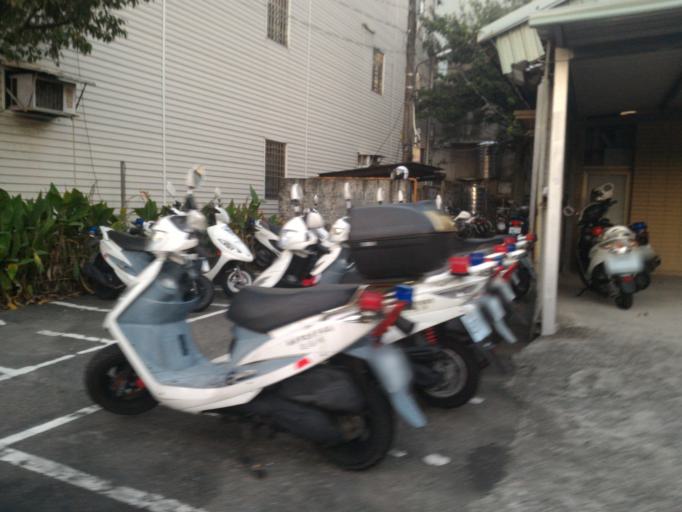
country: TW
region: Taiwan
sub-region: Taoyuan
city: Taoyuan
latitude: 24.9542
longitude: 121.3876
